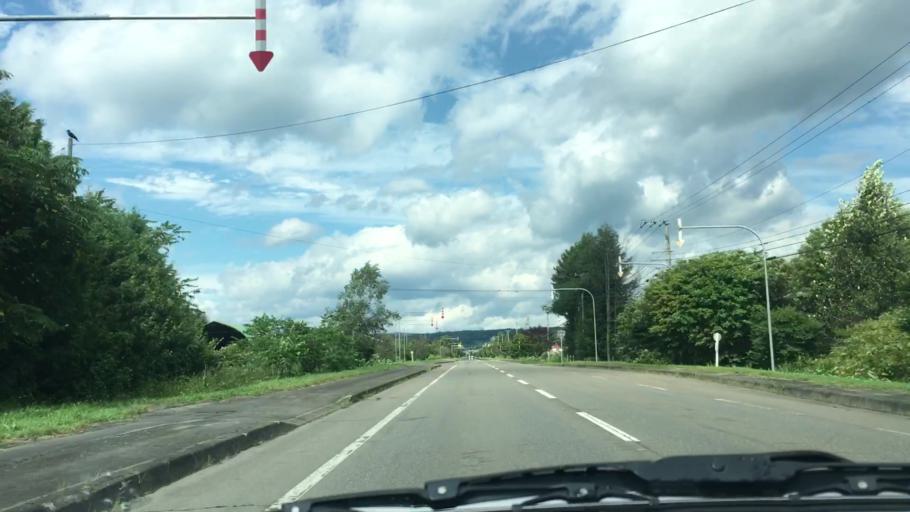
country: JP
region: Hokkaido
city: Otofuke
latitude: 43.2901
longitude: 143.3080
